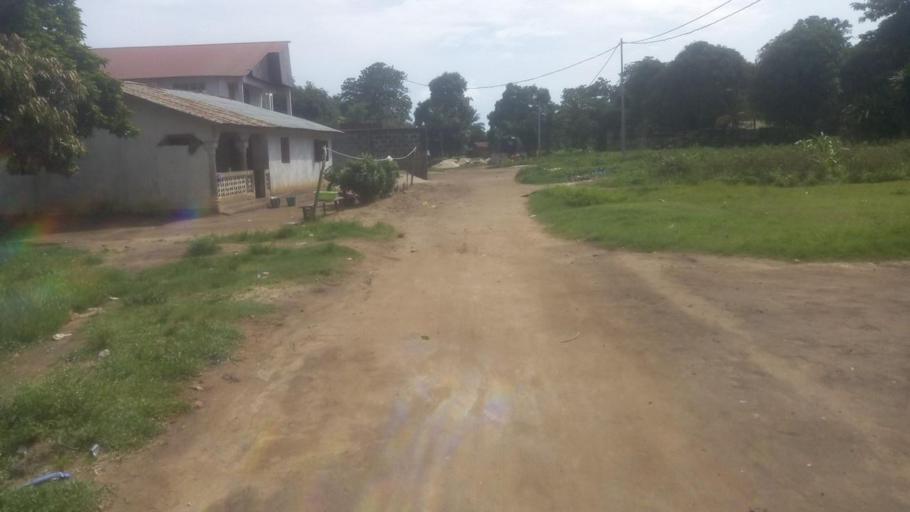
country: SL
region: Northern Province
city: Tintafor
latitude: 8.6342
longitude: -13.2205
